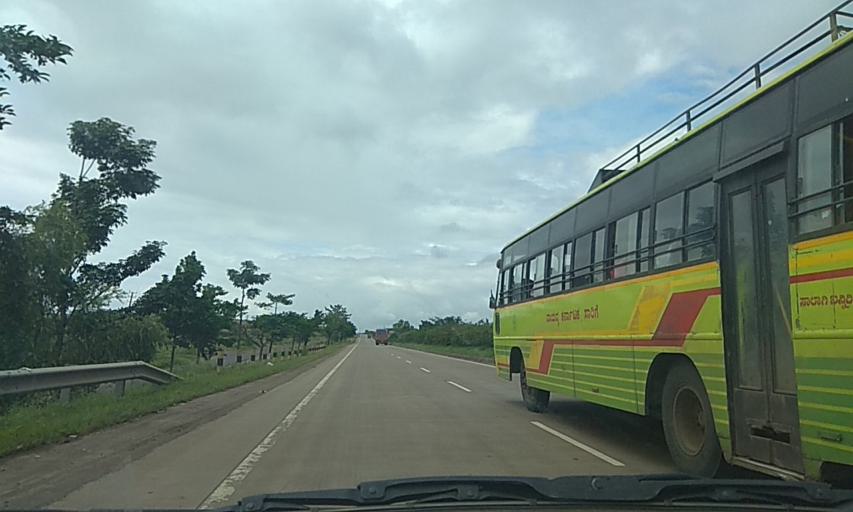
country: IN
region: Maharashtra
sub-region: Kolhapur
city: Kagal
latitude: 16.5189
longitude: 74.3263
